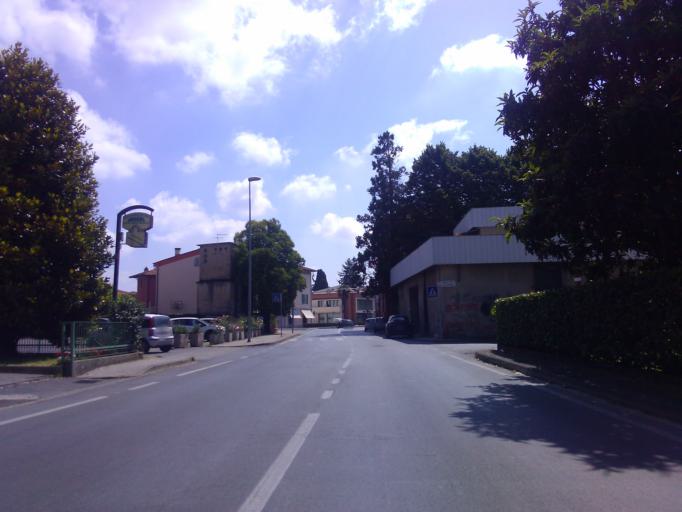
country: IT
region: Tuscany
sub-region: Provincia di Lucca
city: Lucca
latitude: 43.8419
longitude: 10.4894
